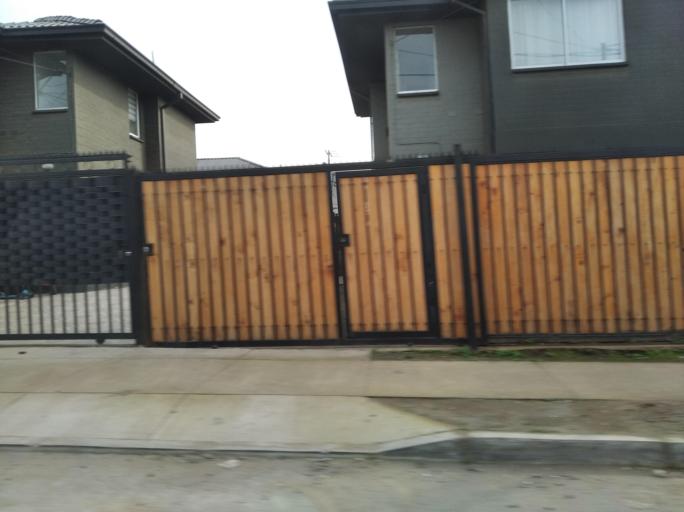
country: CL
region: Santiago Metropolitan
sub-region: Provincia de Chacabuco
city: Lampa
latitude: -33.3018
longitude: -70.8812
